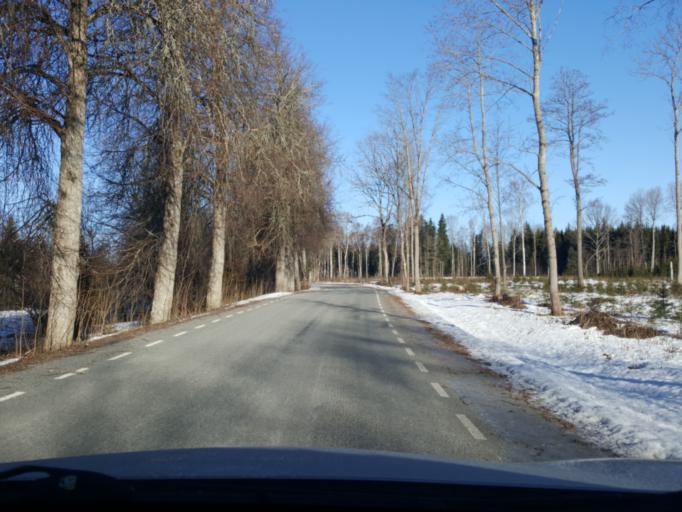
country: EE
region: Viljandimaa
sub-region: Viljandi linn
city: Viljandi
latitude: 58.4210
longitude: 25.5391
